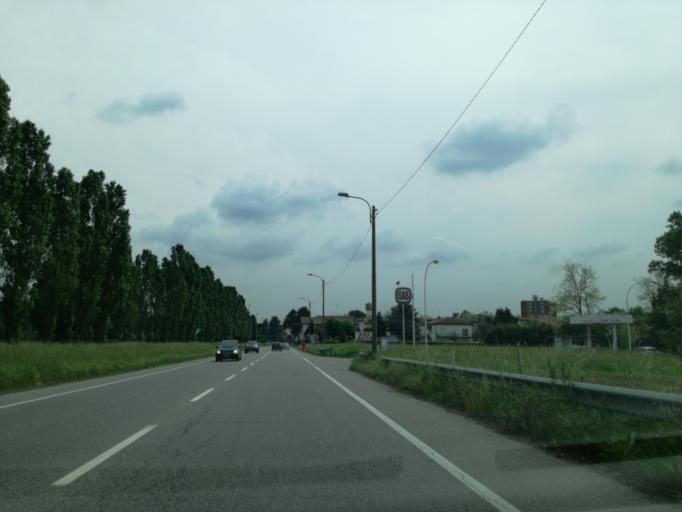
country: IT
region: Lombardy
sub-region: Provincia di Monza e Brianza
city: Albiate
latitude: 45.6637
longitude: 9.2479
